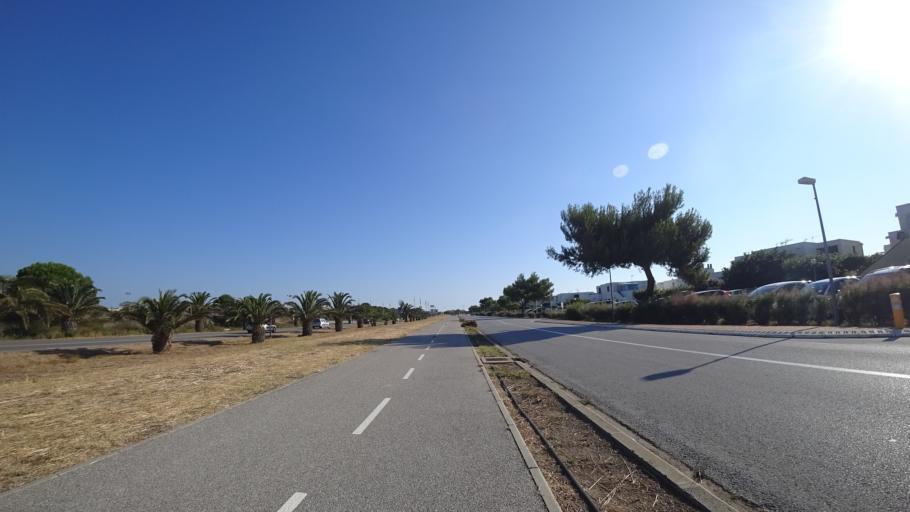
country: FR
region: Languedoc-Roussillon
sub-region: Departement des Pyrenees-Orientales
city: Le Barcares
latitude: 42.8355
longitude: 3.0382
